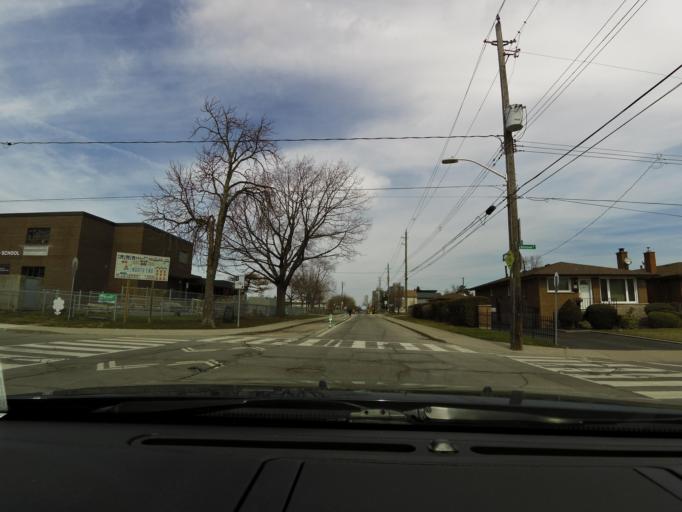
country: CA
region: Ontario
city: Hamilton
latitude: 43.2672
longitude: -79.8616
